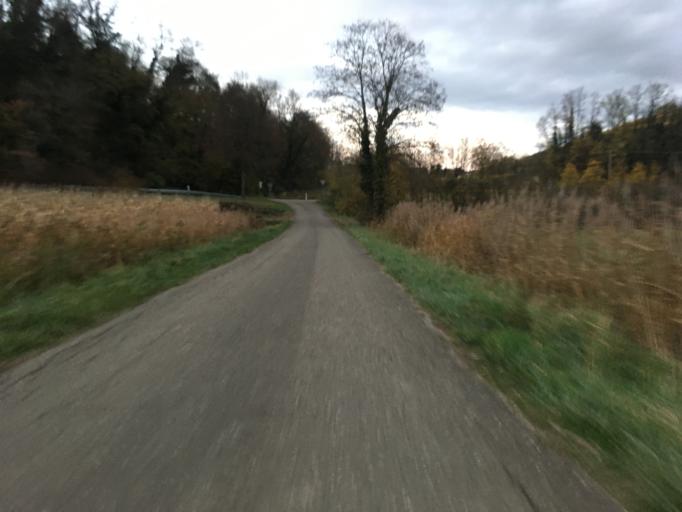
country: DE
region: Baden-Wuerttemberg
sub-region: Freiburg Region
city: Riegel
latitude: 48.1424
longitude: 7.7446
